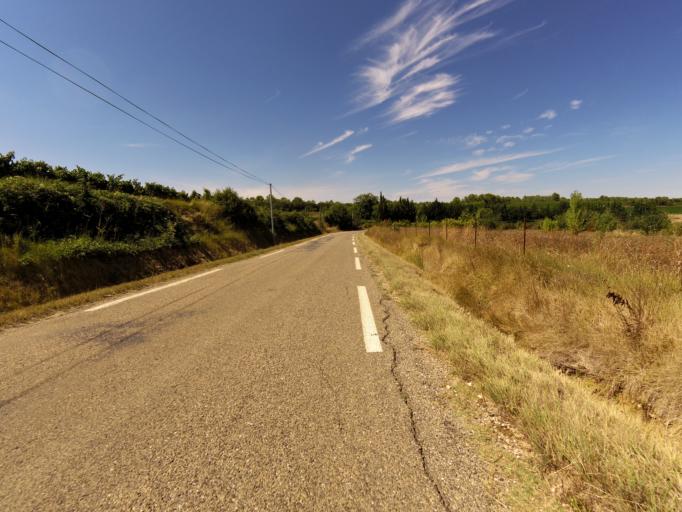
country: FR
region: Languedoc-Roussillon
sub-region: Departement du Gard
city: Sommieres
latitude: 43.8416
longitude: 4.0581
